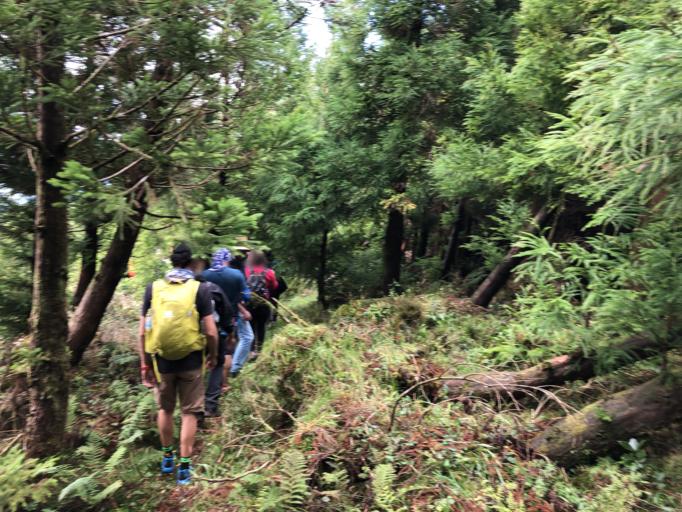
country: PT
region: Azores
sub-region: Ponta Delgada
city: Arrifes
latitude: 37.8330
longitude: -25.7623
